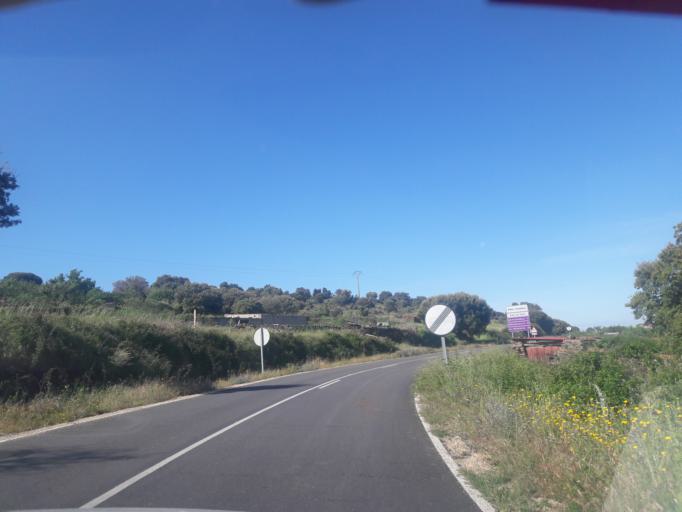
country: ES
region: Castille and Leon
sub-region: Provincia de Salamanca
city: Saucelle
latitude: 41.0445
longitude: -6.7535
